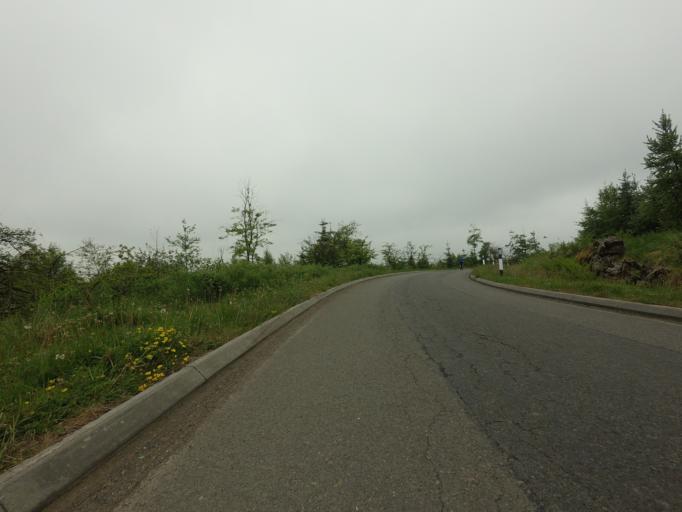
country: GB
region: Scotland
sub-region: Fife
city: Townhill
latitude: 56.1288
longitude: -3.4369
